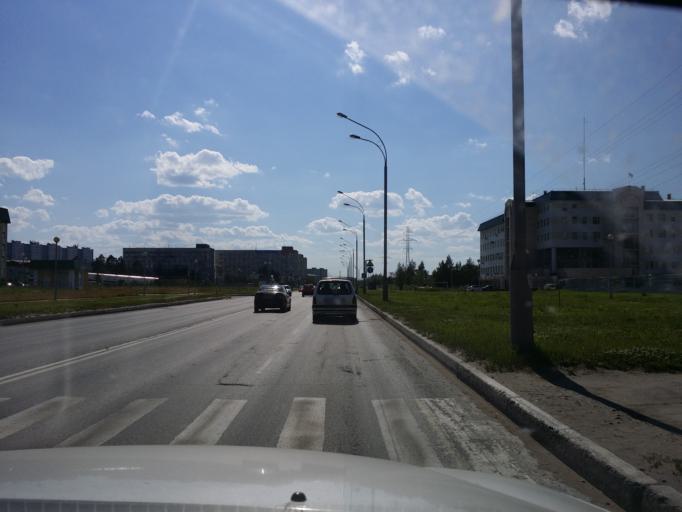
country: RU
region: Khanty-Mansiyskiy Avtonomnyy Okrug
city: Nizhnevartovsk
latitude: 60.9526
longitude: 76.5680
